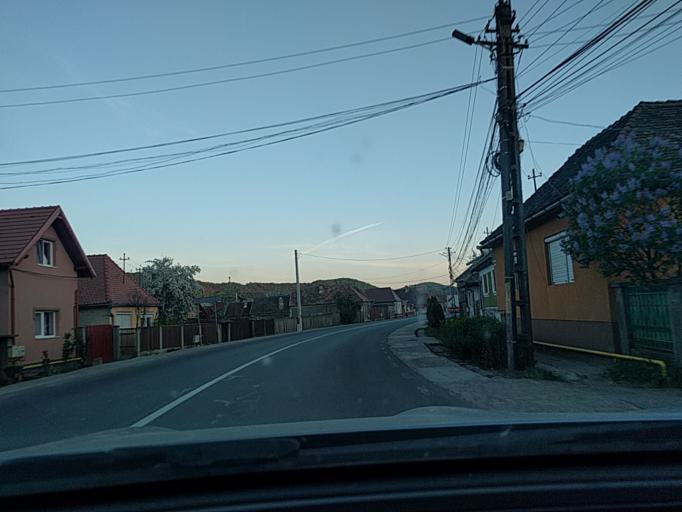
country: RO
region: Mures
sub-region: Comuna Balauseri
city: Chendu
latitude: 46.3899
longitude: 24.7301
